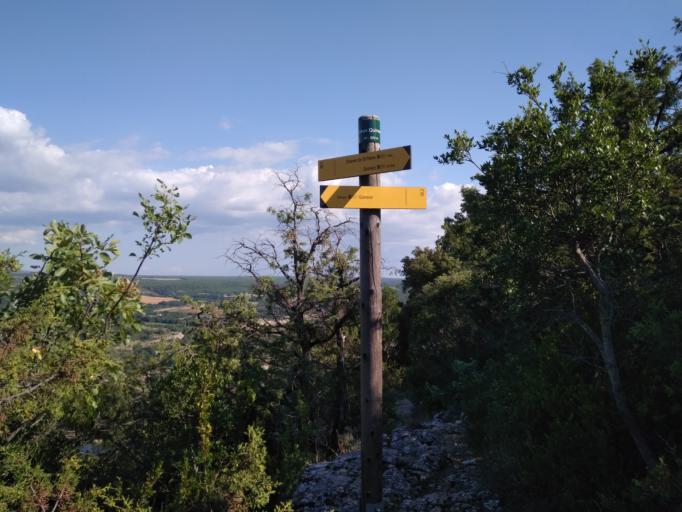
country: FR
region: Provence-Alpes-Cote d'Azur
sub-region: Departement du Var
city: Regusse
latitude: 43.6970
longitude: 6.0328
